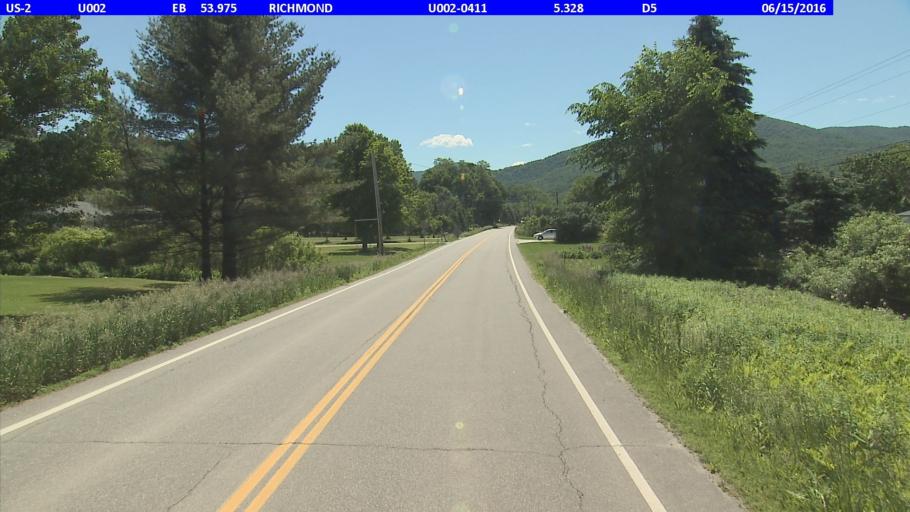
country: US
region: Vermont
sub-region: Chittenden County
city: Jericho
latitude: 44.3935
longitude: -72.9470
